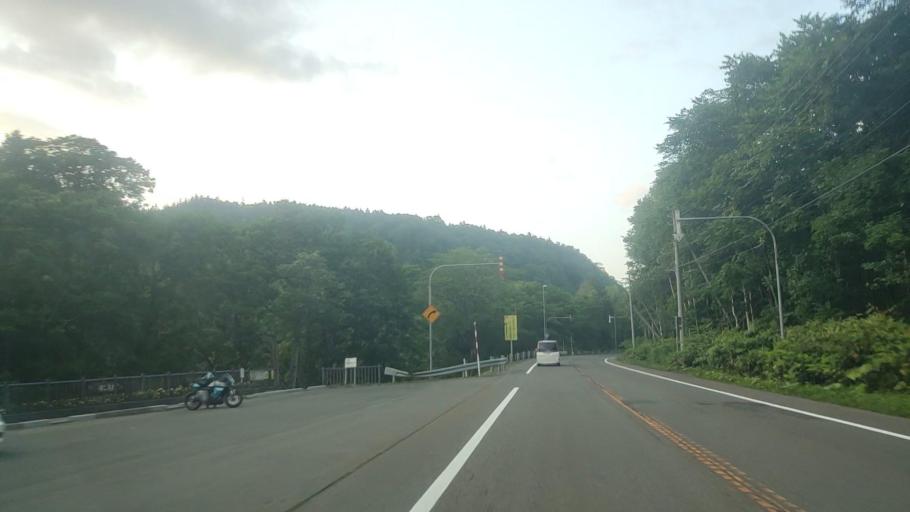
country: JP
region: Hokkaido
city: Ashibetsu
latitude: 43.3492
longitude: 142.1512
